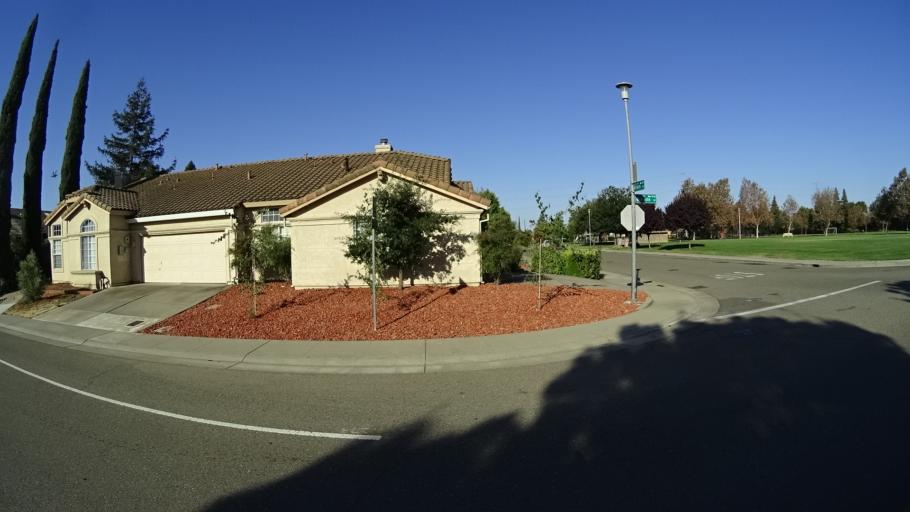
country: US
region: California
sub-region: Sacramento County
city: Laguna
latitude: 38.4217
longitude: -121.4530
